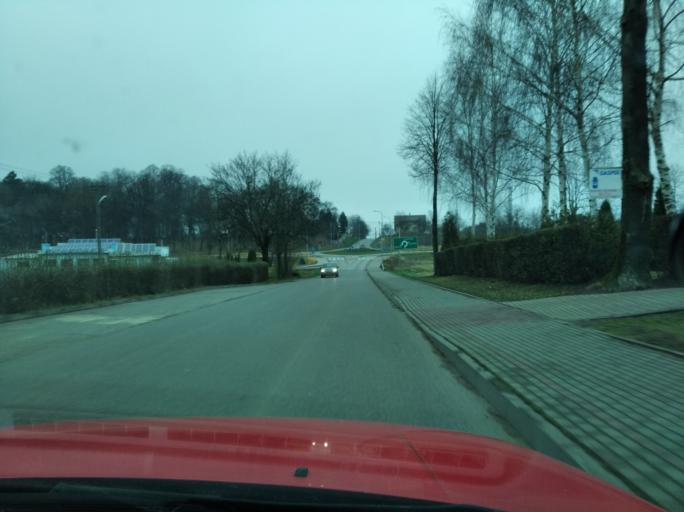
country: PL
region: Subcarpathian Voivodeship
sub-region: Powiat jaroslawski
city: Pawlosiow
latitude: 50.0055
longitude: 22.6567
